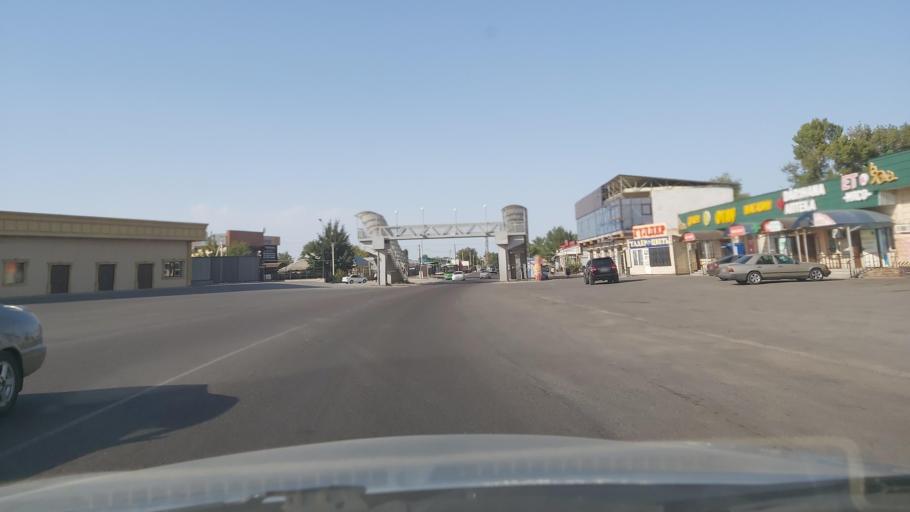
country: KZ
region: Almaty Oblysy
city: Energeticheskiy
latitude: 43.4764
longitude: 77.0311
